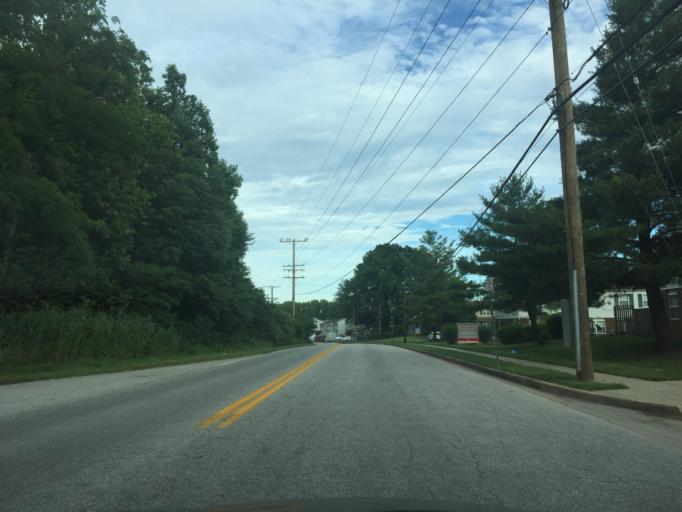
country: US
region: Maryland
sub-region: Baltimore County
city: Bowleys Quarters
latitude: 39.3318
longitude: -76.3859
